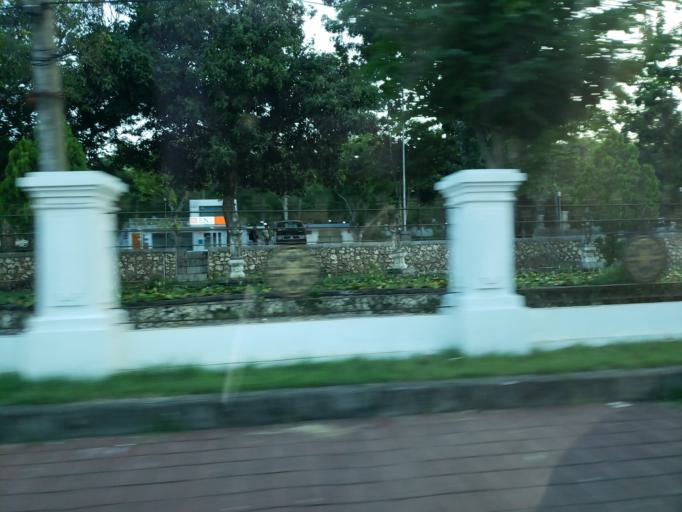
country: ID
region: Bali
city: Jimbaran
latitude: -8.7975
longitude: 115.1715
